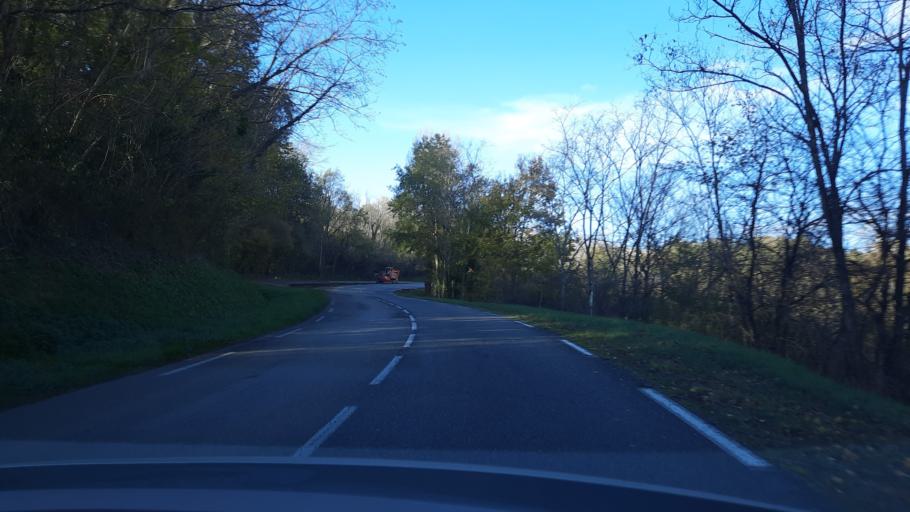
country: FR
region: Midi-Pyrenees
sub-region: Departement du Tarn-et-Garonne
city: Molieres
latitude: 44.1182
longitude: 1.3561
